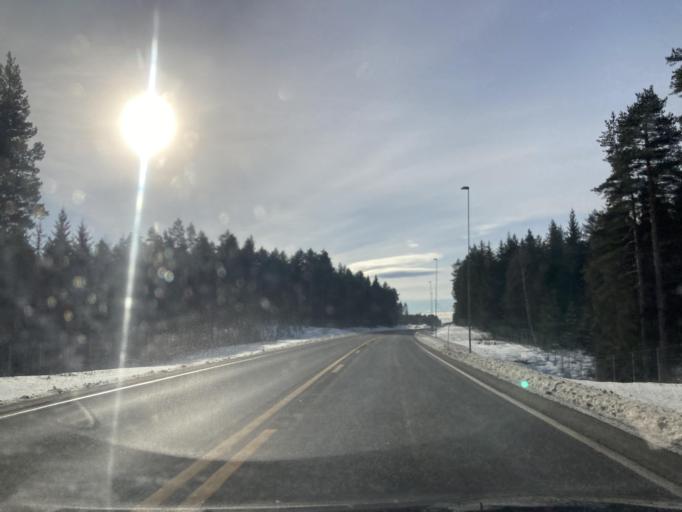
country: NO
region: Hedmark
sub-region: Loten
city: Loten
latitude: 60.7647
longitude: 11.3097
